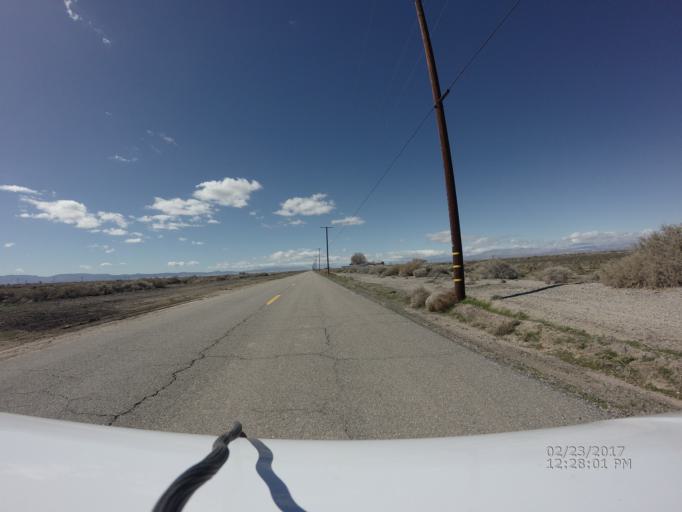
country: US
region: California
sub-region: Los Angeles County
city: Lancaster
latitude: 34.7485
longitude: -118.0335
